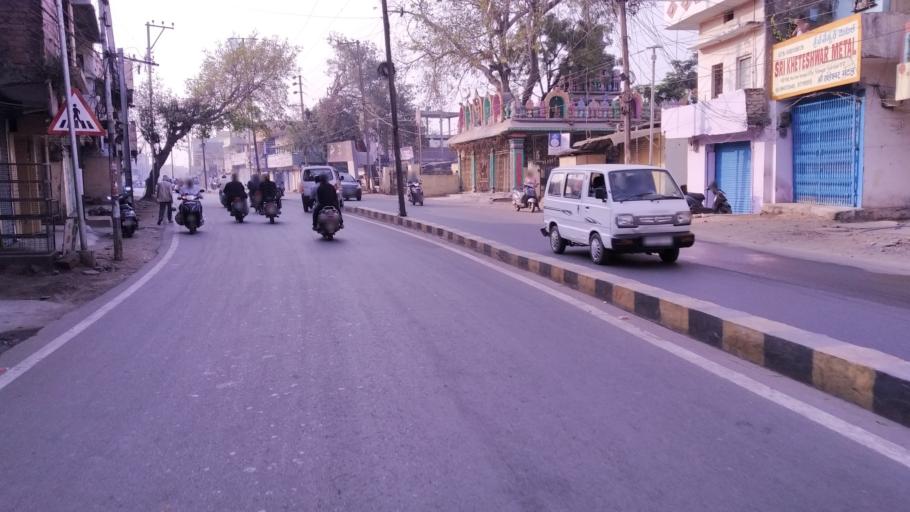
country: IN
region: Telangana
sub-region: Rangareddi
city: Quthbullapur
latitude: 17.4598
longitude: 78.4496
